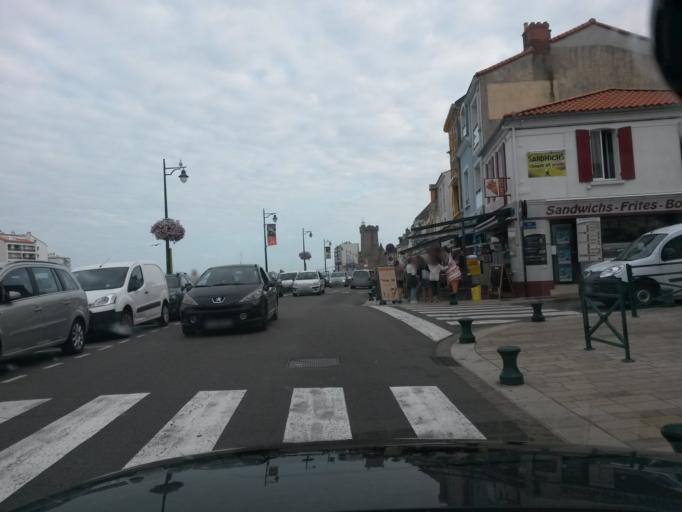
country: FR
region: Pays de la Loire
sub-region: Departement de la Vendee
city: Les Sables-d'Olonne
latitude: 46.4967
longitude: -1.7965
